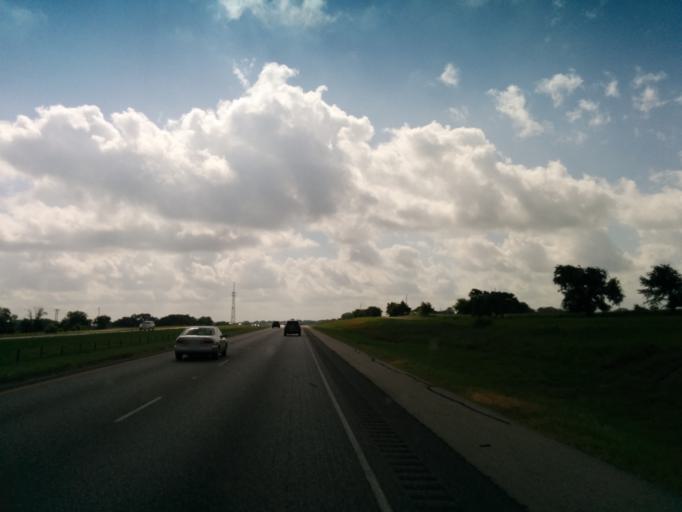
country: US
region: Texas
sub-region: Fayette County
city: Flatonia
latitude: 29.6937
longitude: -97.0210
